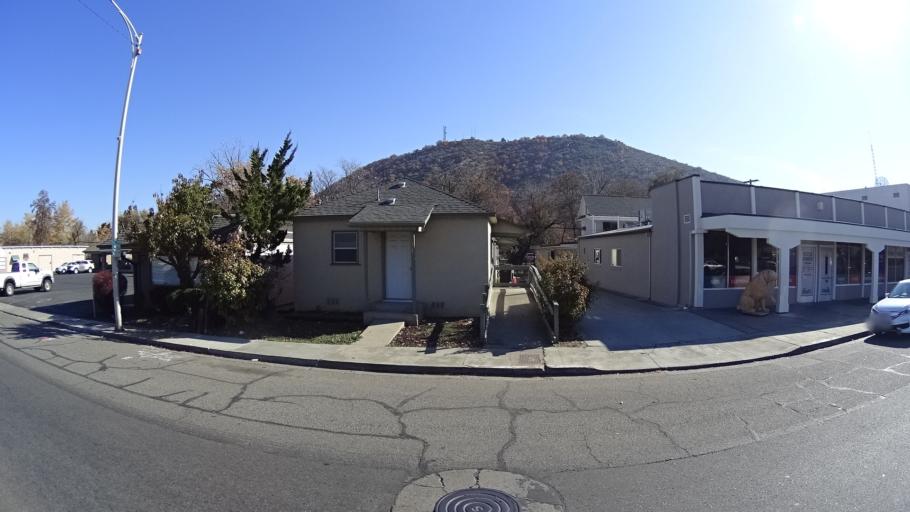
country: US
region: California
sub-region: Siskiyou County
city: Yreka
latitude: 41.7263
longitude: -122.6380
